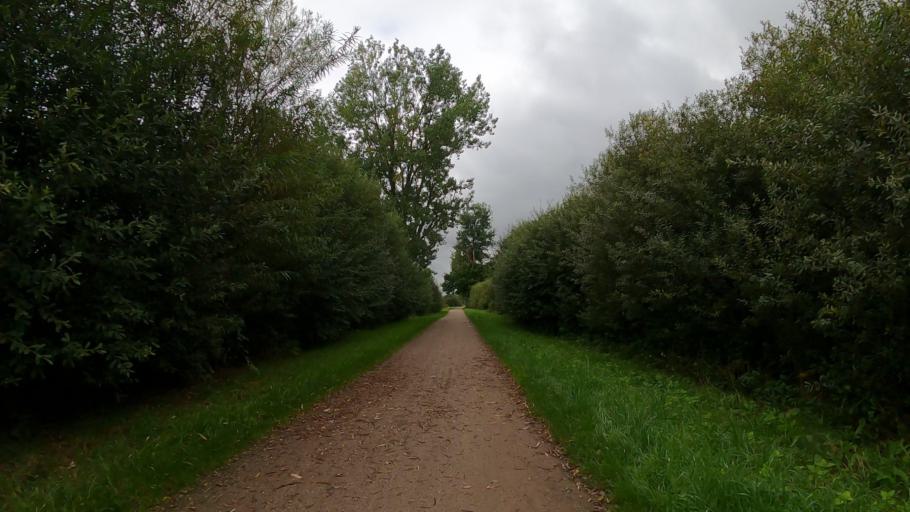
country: DE
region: Lower Saxony
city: Neu Wulmstorf
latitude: 53.4777
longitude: 9.7728
